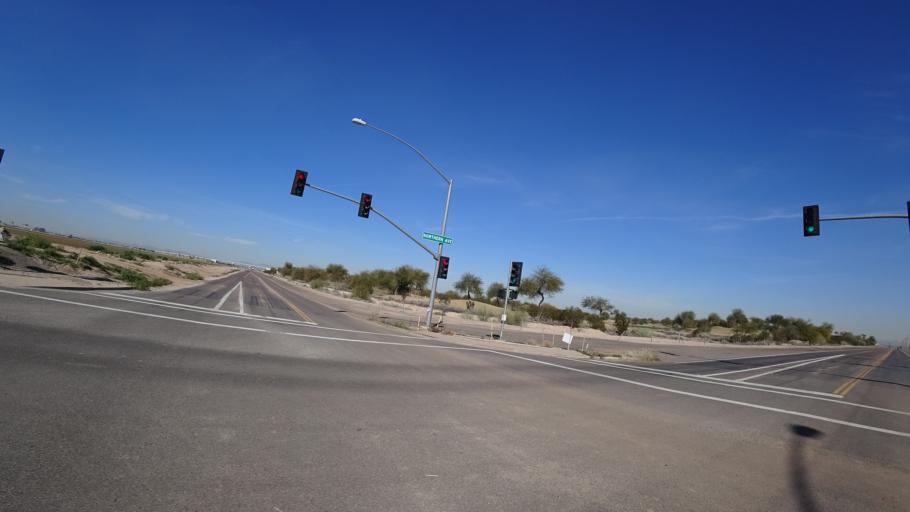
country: US
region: Arizona
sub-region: Maricopa County
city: Citrus Park
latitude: 33.5516
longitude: -112.3936
